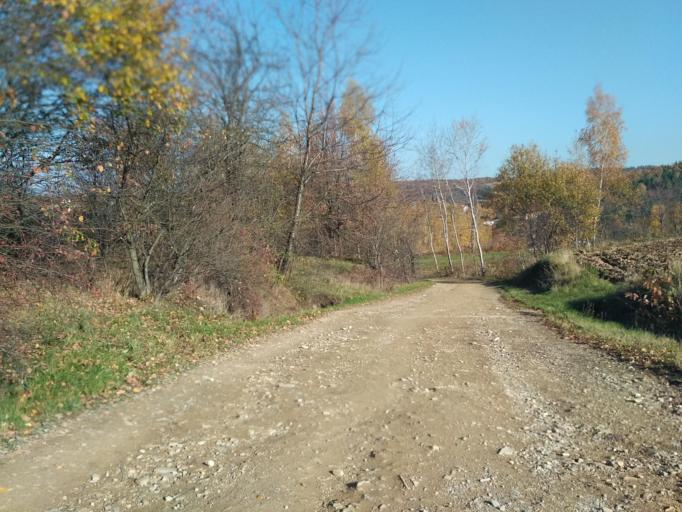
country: PL
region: Subcarpathian Voivodeship
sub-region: Powiat rzeszowski
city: Blazowa
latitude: 49.8763
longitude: 22.0924
